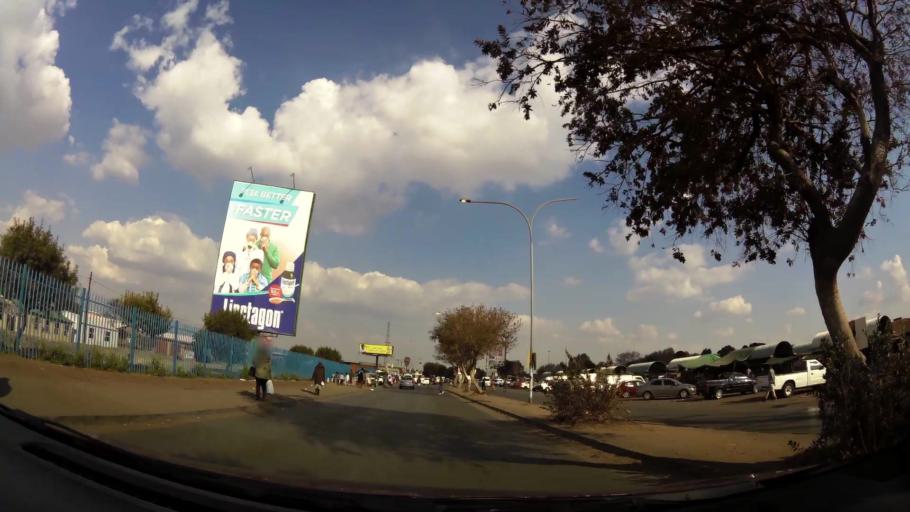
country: ZA
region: Gauteng
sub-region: City of Johannesburg Metropolitan Municipality
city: Roodepoort
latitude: -26.2134
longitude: 27.8708
